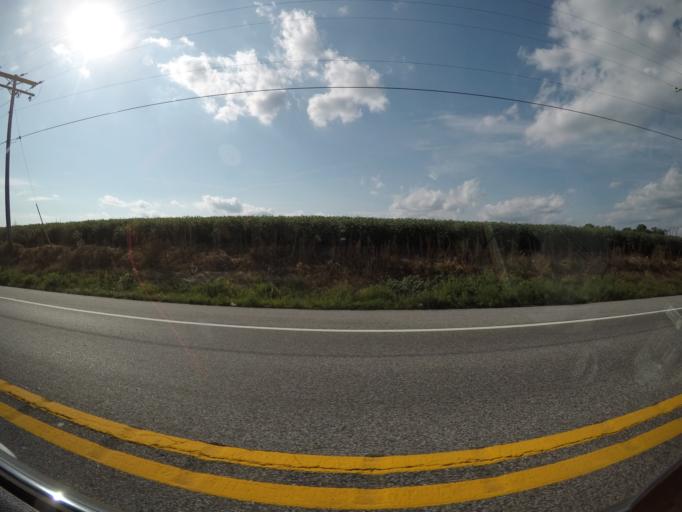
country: US
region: Maryland
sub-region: Harford County
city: North Bel Air
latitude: 39.5883
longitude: -76.3282
